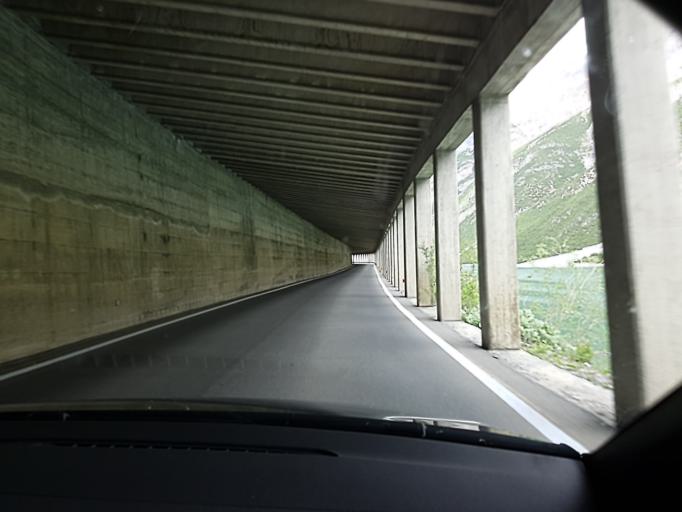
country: IT
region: Lombardy
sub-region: Provincia di Sondrio
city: Livigno
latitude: 46.5720
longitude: 10.1632
